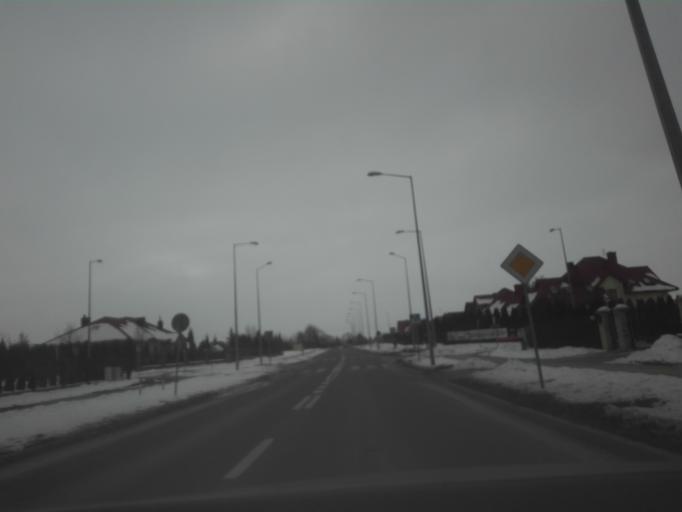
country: PL
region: Lublin Voivodeship
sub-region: Powiat hrubieszowski
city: Hrubieszow
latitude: 50.7984
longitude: 23.8965
